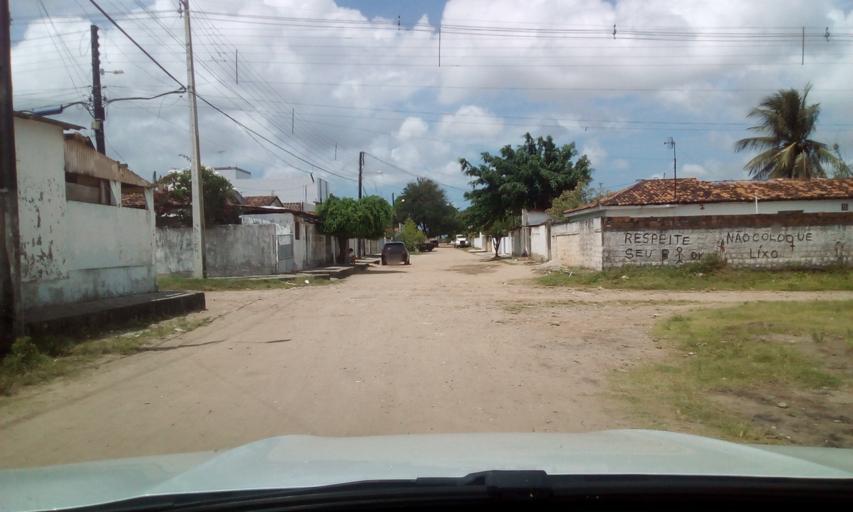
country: BR
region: Paraiba
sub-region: Bayeux
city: Bayeux
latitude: -7.1796
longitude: -34.9186
